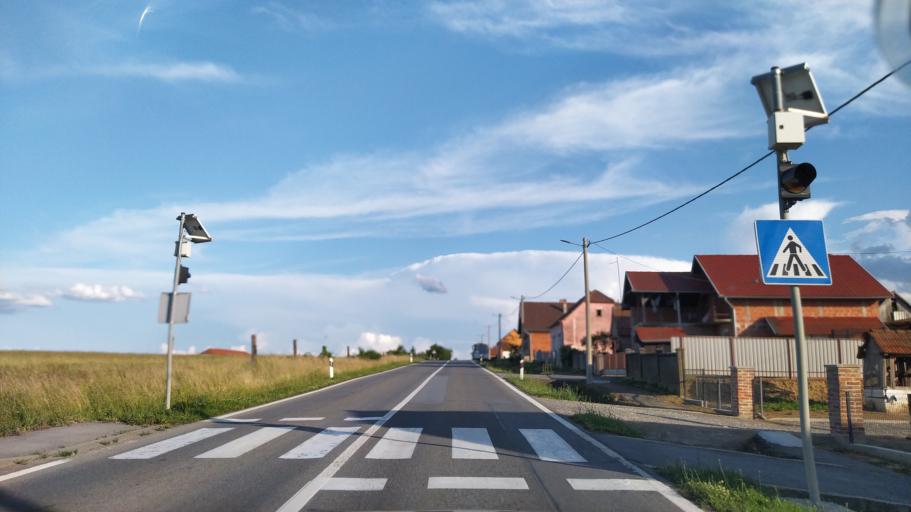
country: HR
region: Virovitick-Podravska
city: Slatina
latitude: 45.6554
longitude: 17.7759
